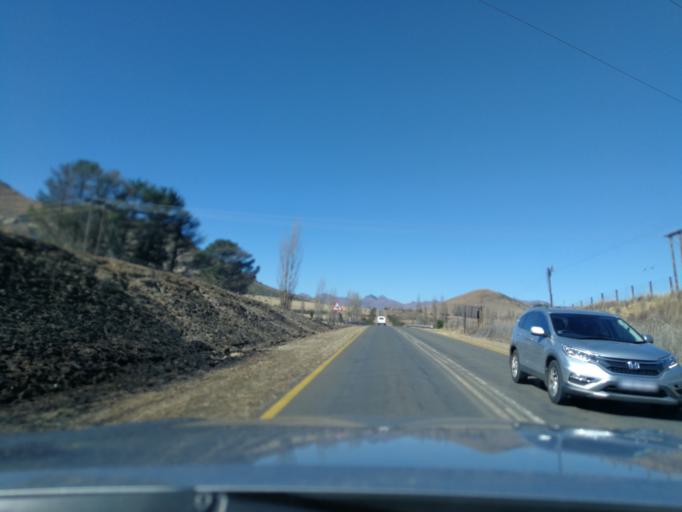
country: ZA
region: Orange Free State
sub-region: Thabo Mofutsanyana District Municipality
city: Bethlehem
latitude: -28.5153
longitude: 28.4349
